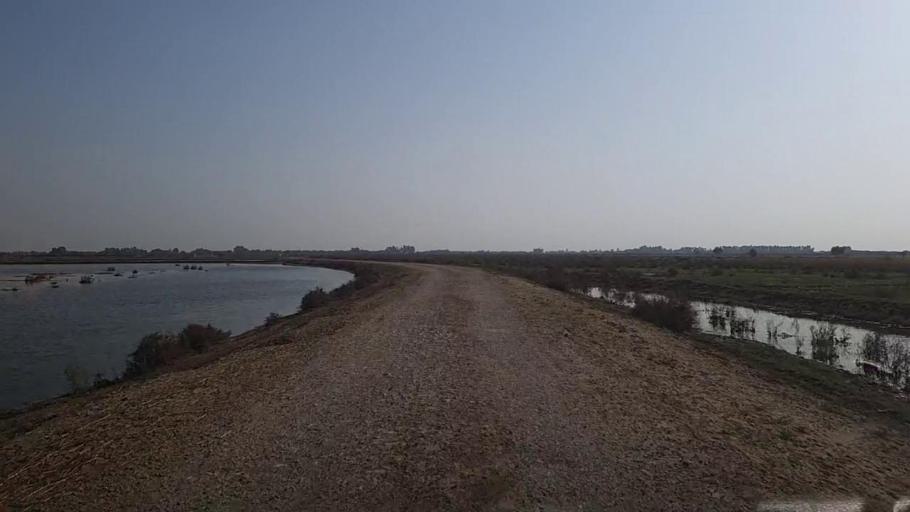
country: PK
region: Sindh
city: Kandhkot
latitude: 28.3657
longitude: 69.3297
